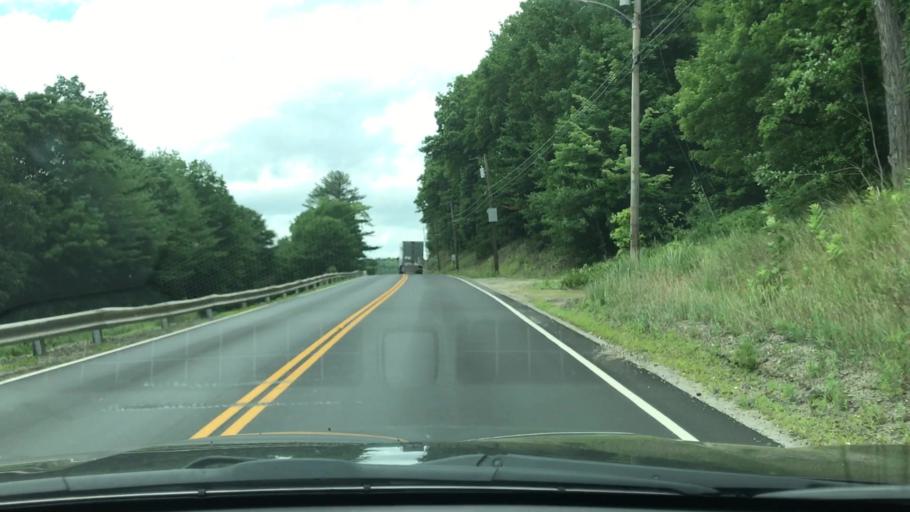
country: US
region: Maine
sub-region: Oxford County
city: West Paris
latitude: 44.3817
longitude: -70.6505
